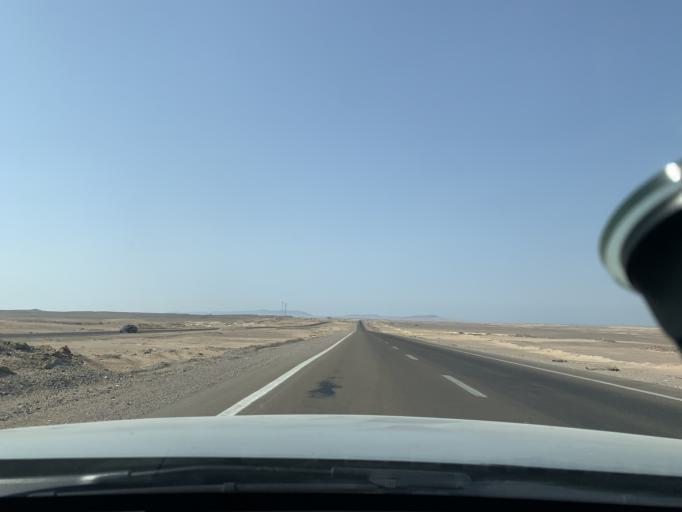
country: EG
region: Red Sea
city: El Gouna
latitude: 27.6989
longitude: 33.4992
